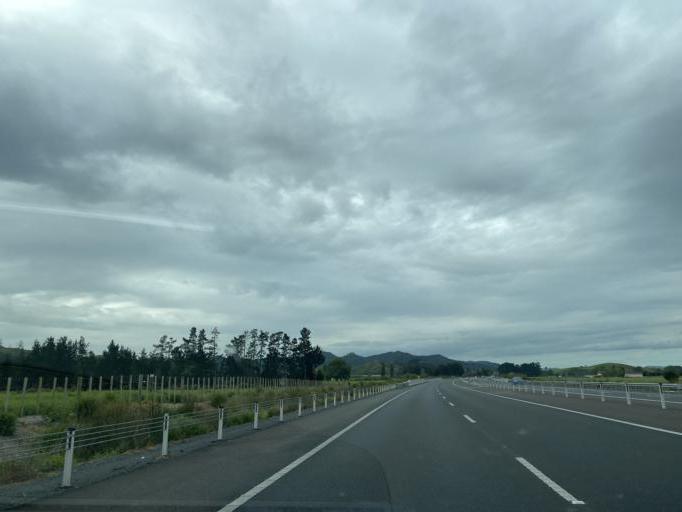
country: NZ
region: Waikato
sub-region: Waikato District
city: Ngaruawahia
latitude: -37.6081
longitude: 175.2047
